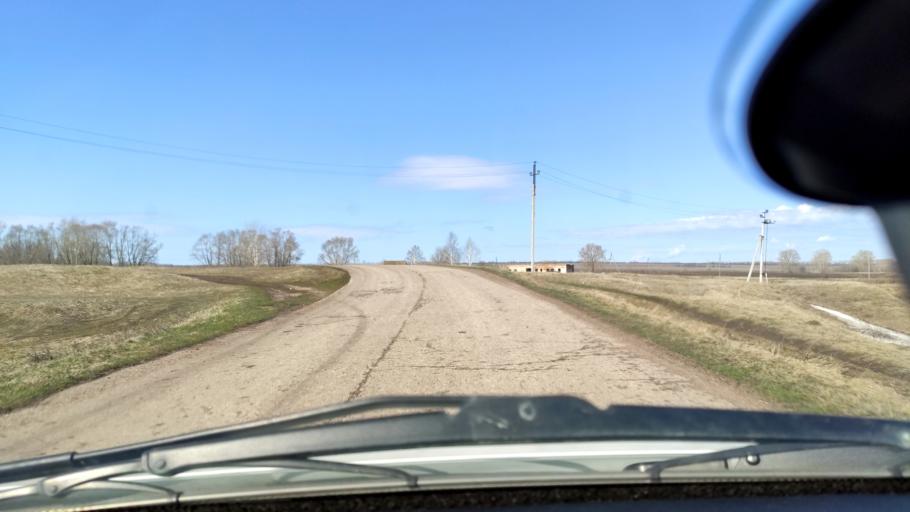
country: RU
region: Bashkortostan
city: Tolbazy
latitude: 54.1729
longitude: 55.9495
